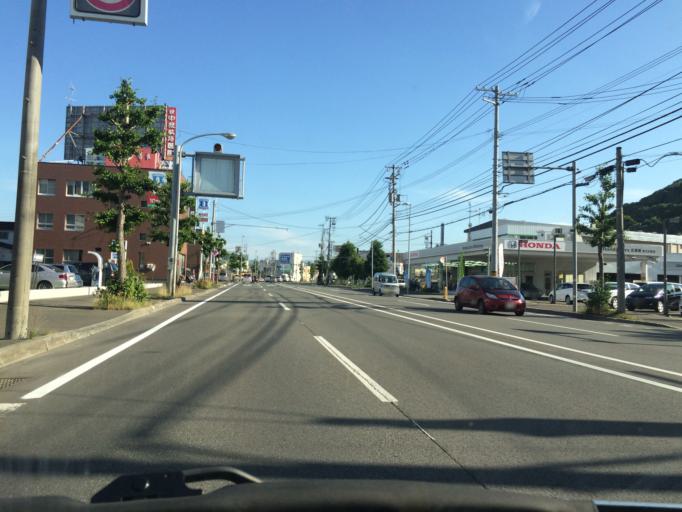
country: JP
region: Hokkaido
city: Sapporo
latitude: 43.0166
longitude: 141.3467
